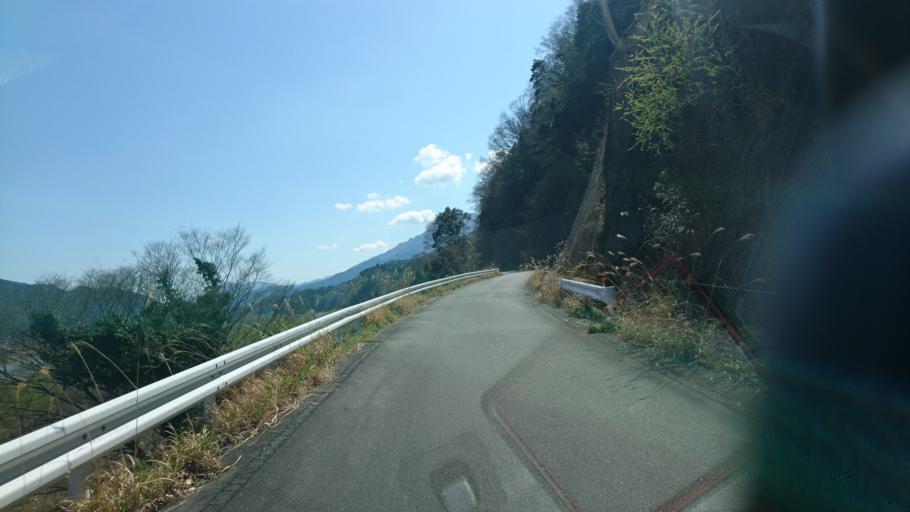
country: JP
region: Shizuoka
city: Fujinomiya
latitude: 35.3332
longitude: 138.4436
